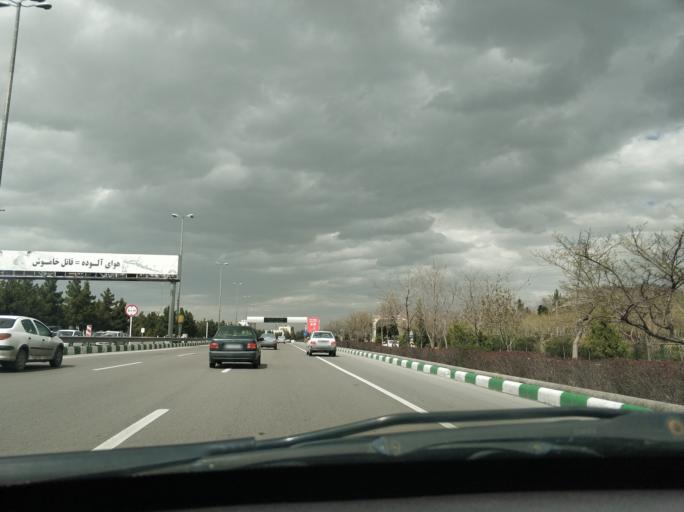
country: IR
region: Razavi Khorasan
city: Mashhad
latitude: 36.2754
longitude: 59.5551
